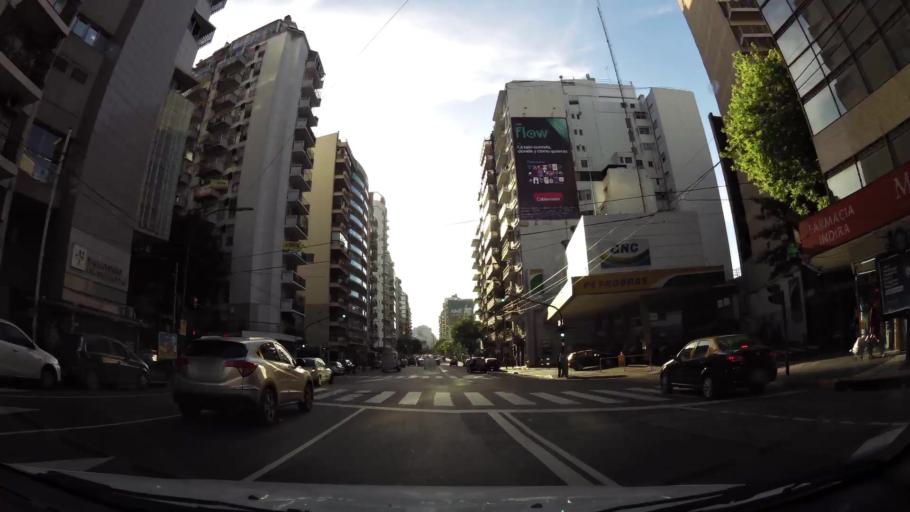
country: AR
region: Buenos Aires F.D.
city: Retiro
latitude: -34.5981
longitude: -58.4054
